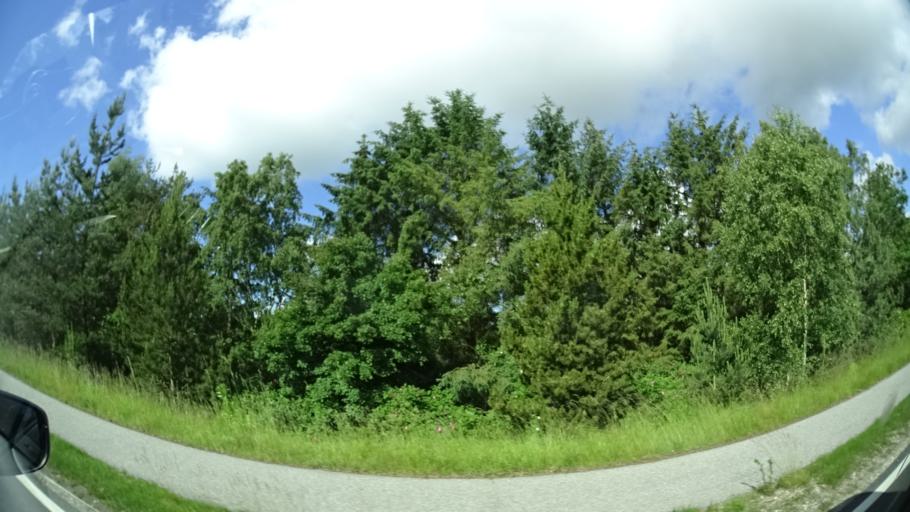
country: DK
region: Central Jutland
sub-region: Syddjurs Kommune
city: Ebeltoft
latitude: 56.2282
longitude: 10.6613
